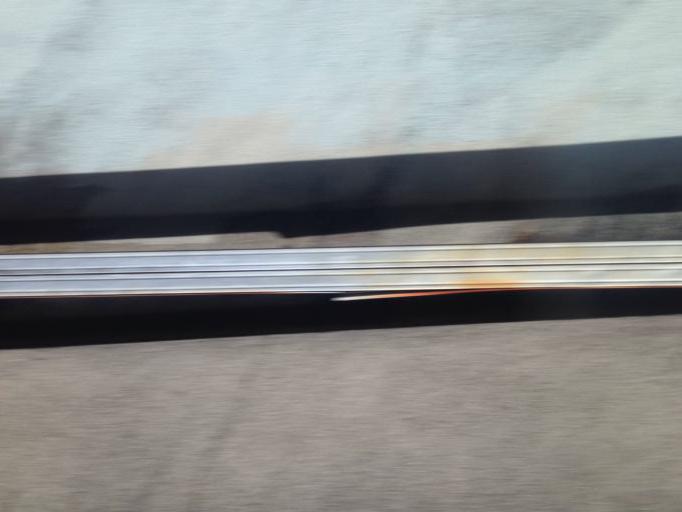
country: AU
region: New South Wales
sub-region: City of Sydney
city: Sydney
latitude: -33.8580
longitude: 151.2069
